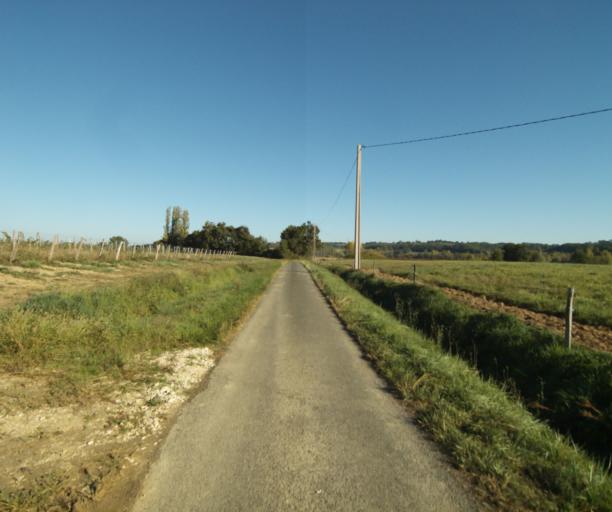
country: FR
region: Midi-Pyrenees
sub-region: Departement du Gers
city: Gondrin
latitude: 43.8453
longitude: 0.2330
